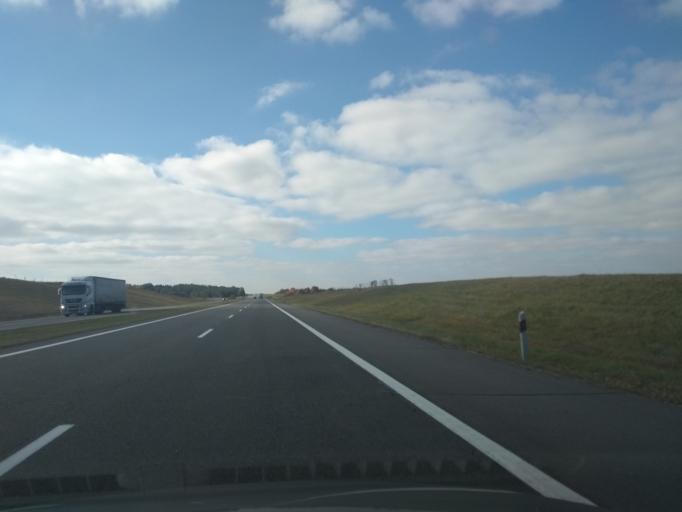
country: BY
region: Minsk
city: Snow
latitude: 53.2652
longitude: 26.2791
